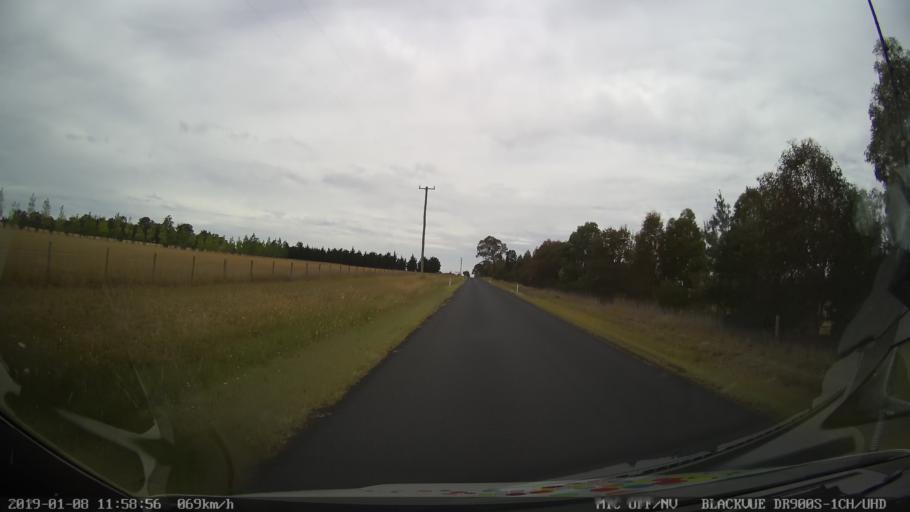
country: AU
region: New South Wales
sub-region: Armidale Dumaresq
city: Armidale
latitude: -30.4578
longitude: 151.5810
